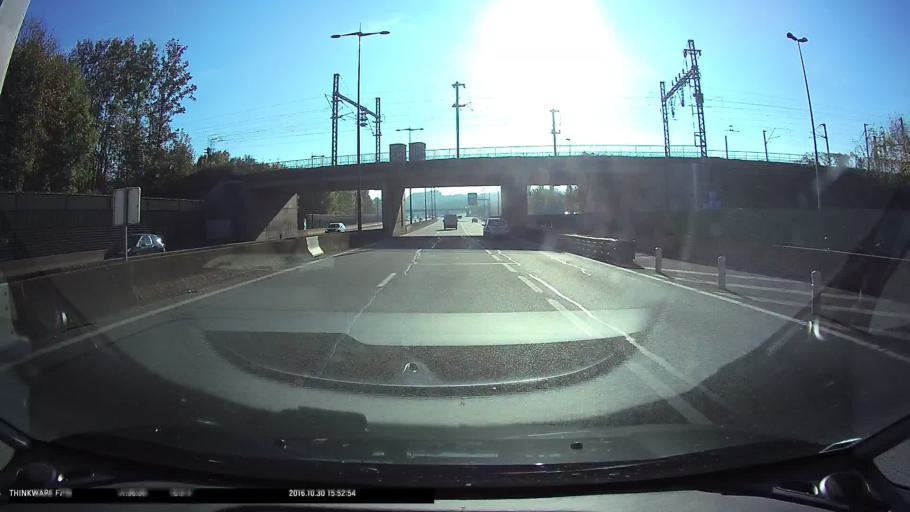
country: FR
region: Franche-Comte
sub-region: Territoire de Belfort
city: Danjoutin
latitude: 47.6236
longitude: 6.8615
